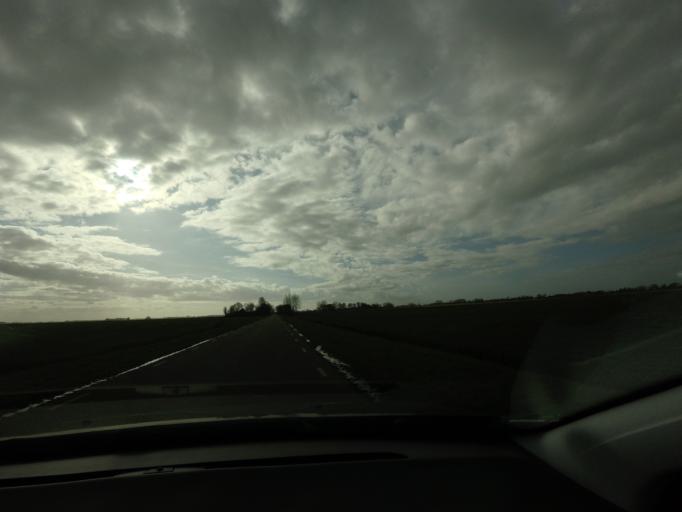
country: NL
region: Friesland
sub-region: Gemeente Boarnsterhim
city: Jirnsum
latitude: 53.0688
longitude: 5.7599
